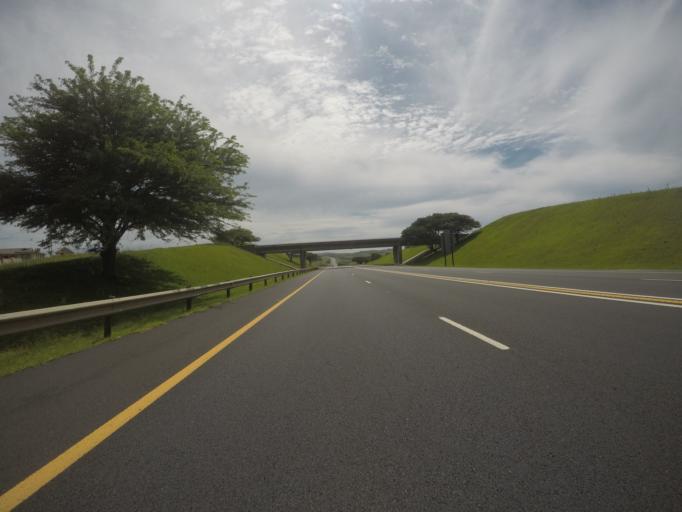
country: ZA
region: KwaZulu-Natal
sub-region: iLembe District Municipality
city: Mandeni
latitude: -29.1733
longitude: 31.5137
